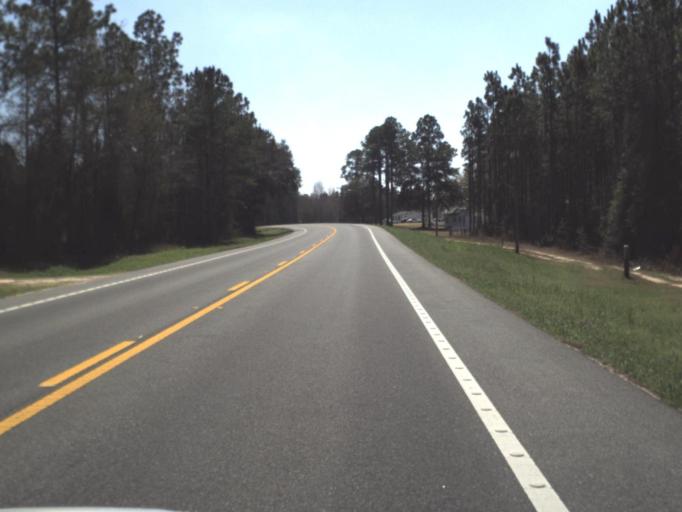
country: US
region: Florida
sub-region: Jackson County
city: Sneads
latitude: 30.6397
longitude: -85.0377
